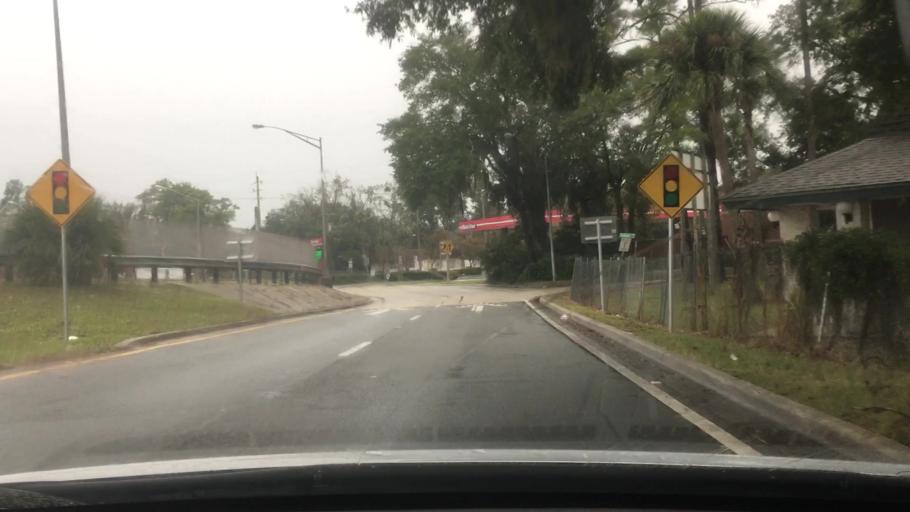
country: US
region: Florida
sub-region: Duval County
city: Jacksonville
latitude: 30.3076
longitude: -81.6173
